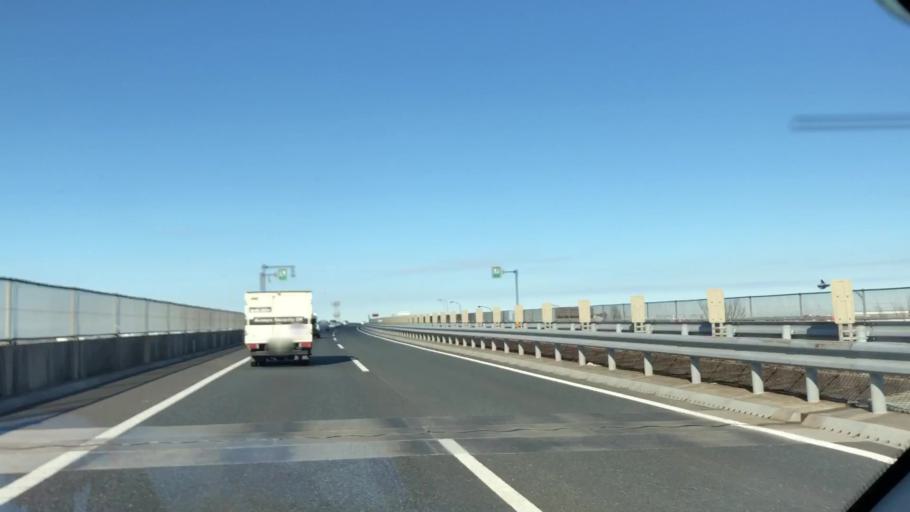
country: JP
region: Chiba
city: Kisarazu
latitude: 35.4224
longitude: 139.9352
